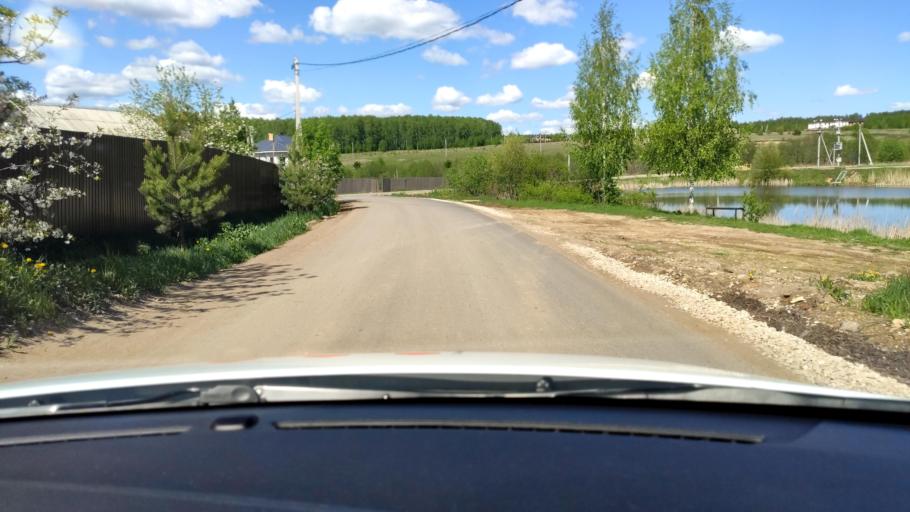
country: RU
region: Tatarstan
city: Vysokaya Gora
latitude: 55.8180
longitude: 49.2820
